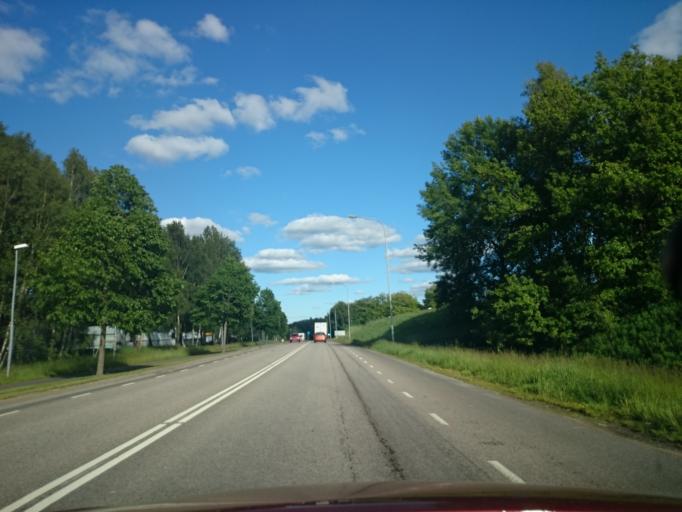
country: SE
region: Vaestra Goetaland
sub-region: Harryda Kommun
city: Molnlycke
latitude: 57.6690
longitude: 12.0923
